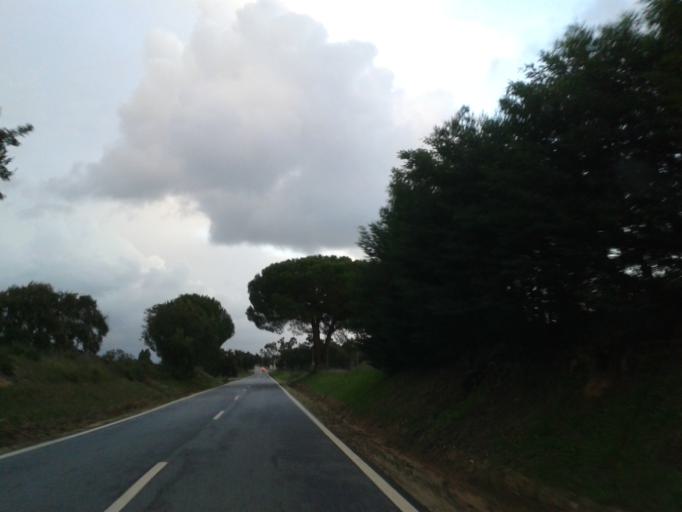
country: PT
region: Santarem
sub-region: Benavente
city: Poceirao
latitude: 38.8353
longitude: -8.7411
